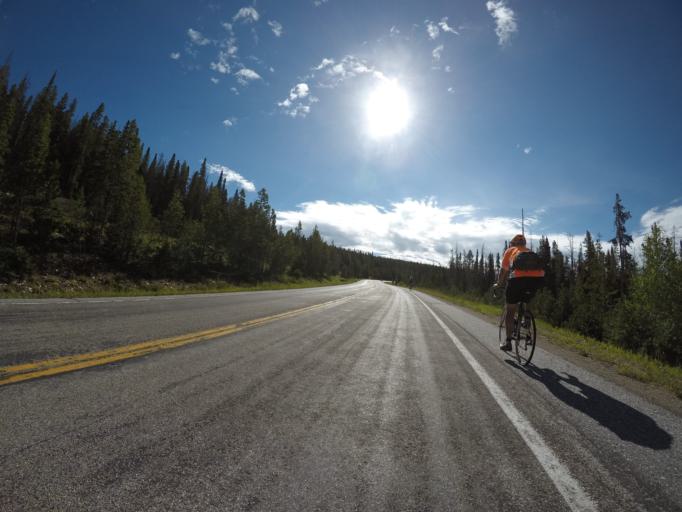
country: US
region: Wyoming
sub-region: Carbon County
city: Saratoga
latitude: 41.3256
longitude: -106.4661
